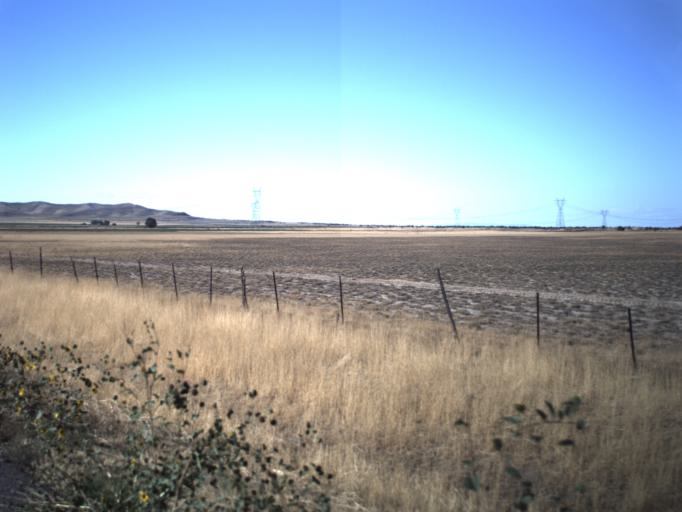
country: US
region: Utah
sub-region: Millard County
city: Delta
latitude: 39.5019
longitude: -112.2690
